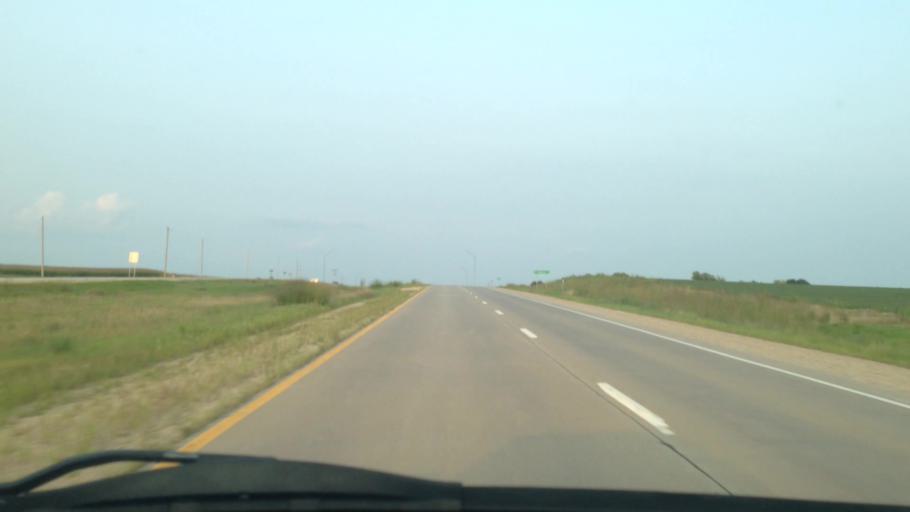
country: US
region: Iowa
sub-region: Benton County
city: Atkins
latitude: 41.9632
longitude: -91.9754
